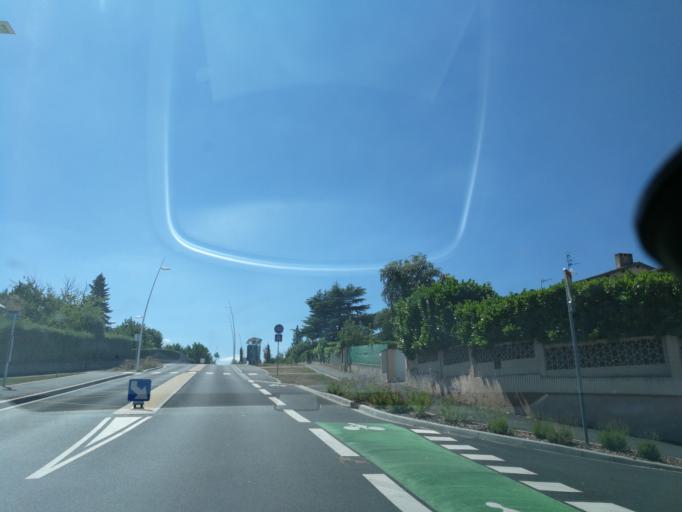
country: FR
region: Midi-Pyrenees
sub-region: Departement de la Haute-Garonne
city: Balma
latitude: 43.6095
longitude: 1.5029
